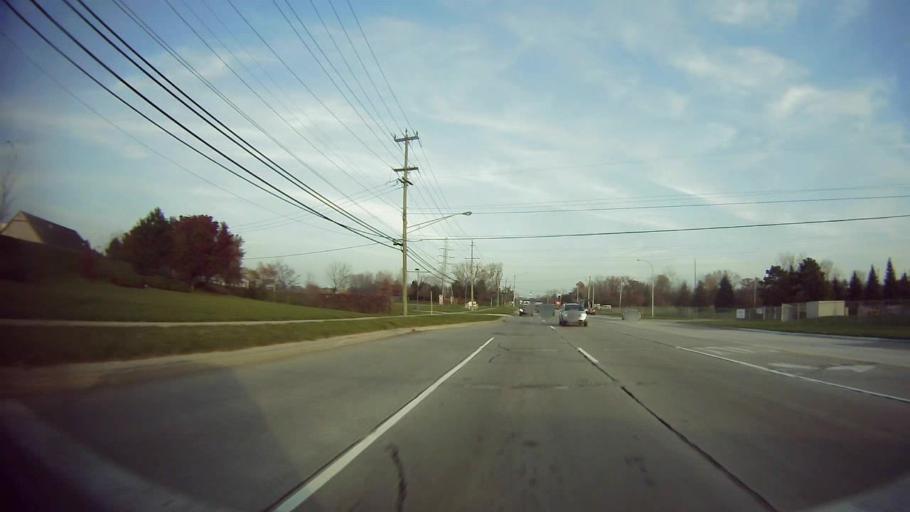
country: US
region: Michigan
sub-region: Oakland County
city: Madison Heights
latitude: 42.5204
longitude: -83.0953
